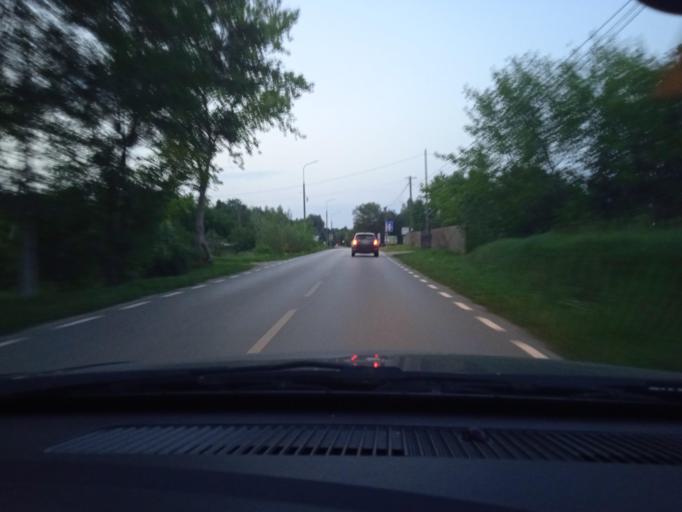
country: PL
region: Masovian Voivodeship
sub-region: Powiat nowodworski
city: Pomiechowek
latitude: 52.5181
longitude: 20.6801
